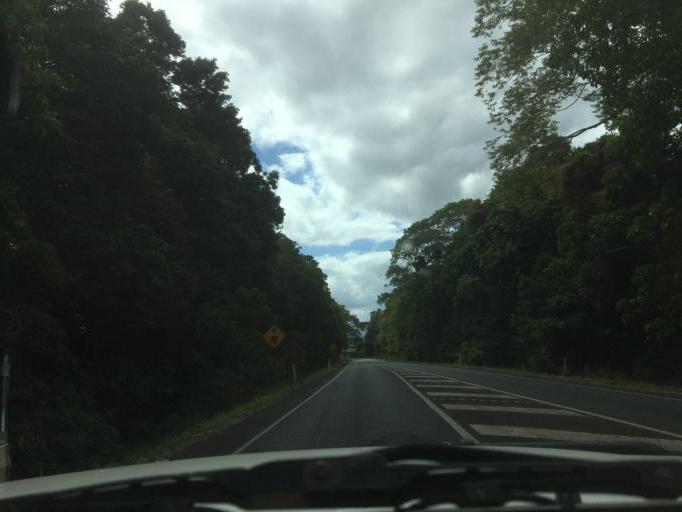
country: AU
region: Queensland
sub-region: Tablelands
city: Atherton
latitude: -17.2826
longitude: 145.6122
